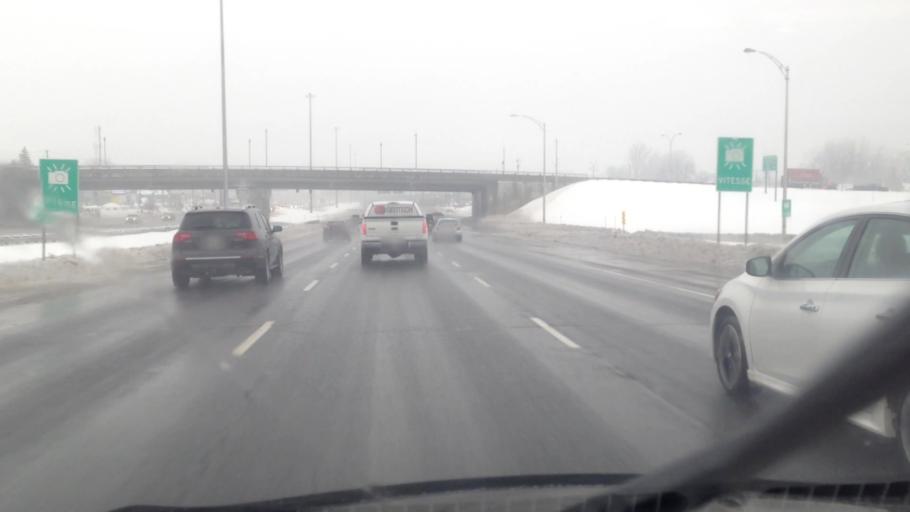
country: CA
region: Quebec
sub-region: Laurentides
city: Boisbriand
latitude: 45.5986
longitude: -73.8040
